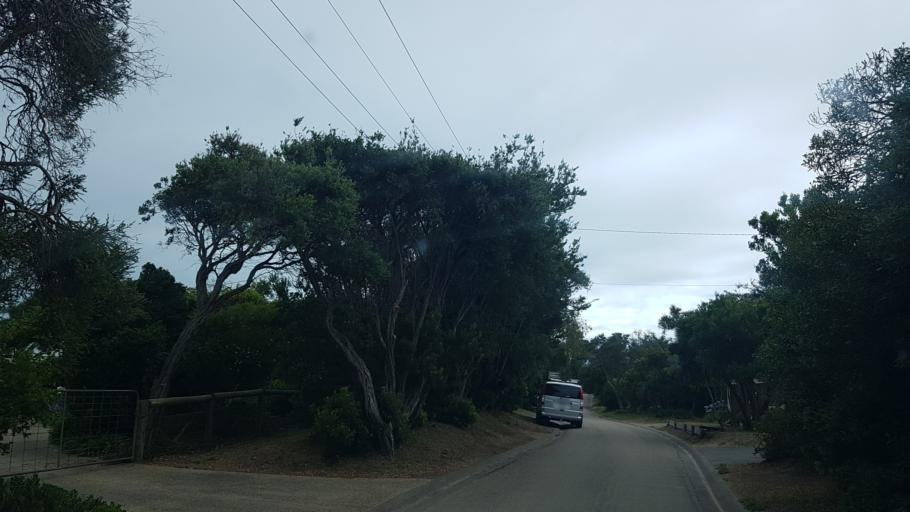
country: AU
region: Victoria
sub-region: Mornington Peninsula
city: Blairgowrie
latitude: -38.3775
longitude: 144.7789
